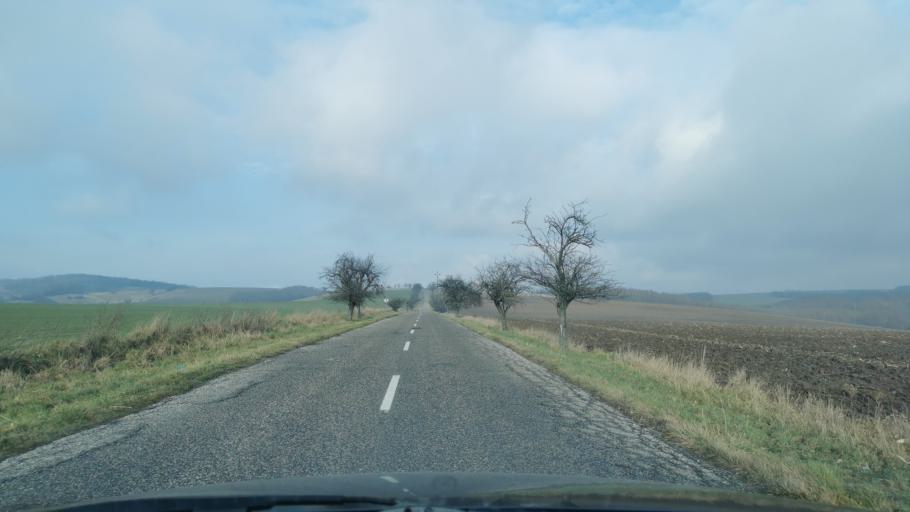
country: SK
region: Trnavsky
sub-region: Okres Senica
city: Senica
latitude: 48.7187
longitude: 17.3224
